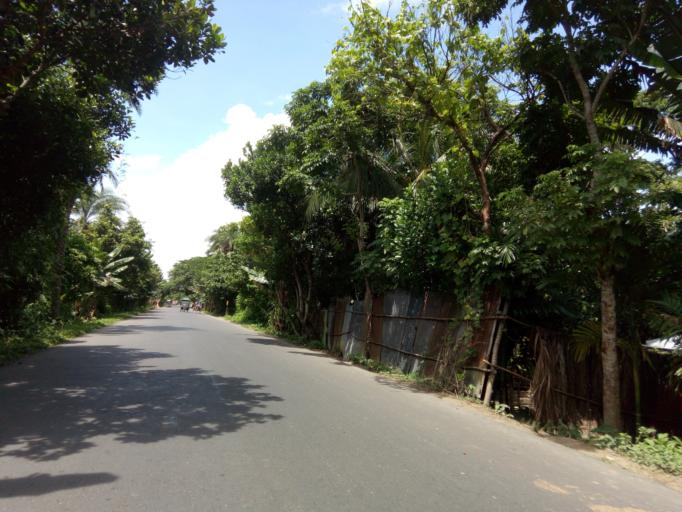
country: BD
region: Dhaka
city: Tungipara
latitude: 22.9009
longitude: 89.8868
